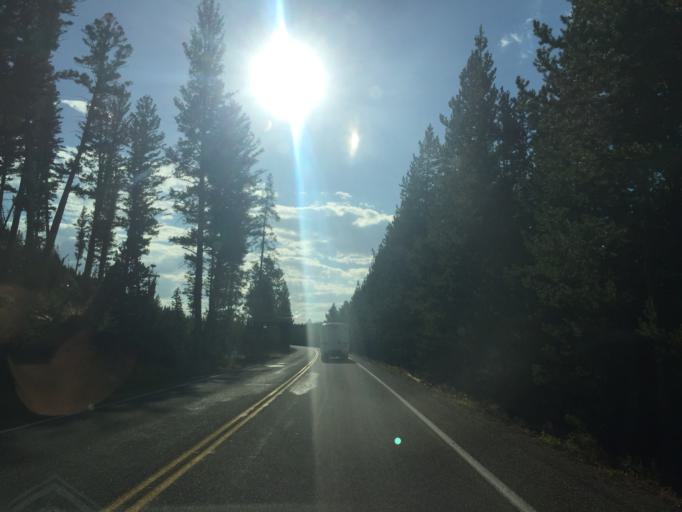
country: US
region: Montana
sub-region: Gallatin County
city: West Yellowstone
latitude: 44.6670
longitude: -110.9858
